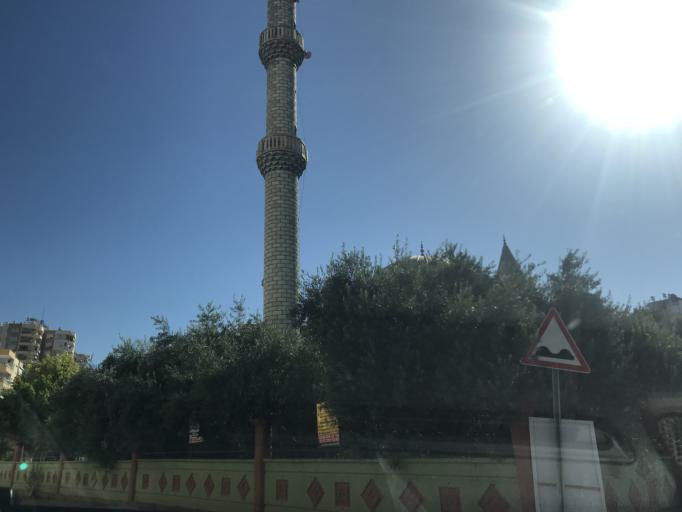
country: TR
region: Antalya
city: Antalya
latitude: 36.8929
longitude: 30.6295
